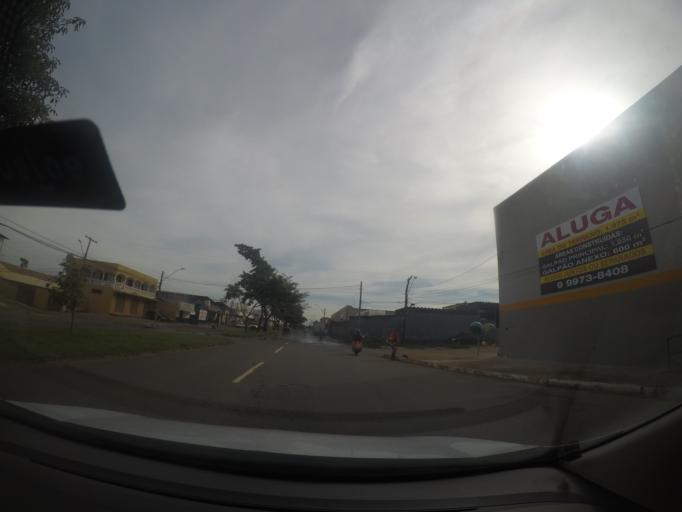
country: BR
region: Goias
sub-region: Goiania
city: Goiania
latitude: -16.6745
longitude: -49.3164
